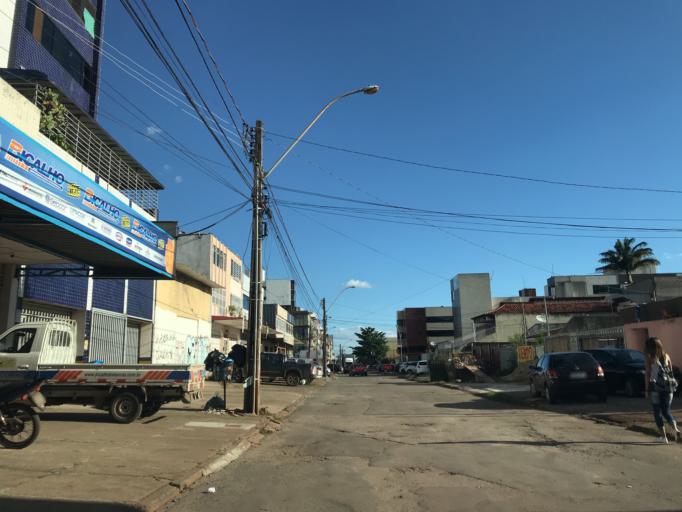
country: BR
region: Federal District
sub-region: Brasilia
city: Brasilia
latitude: -15.8085
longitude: -48.0647
